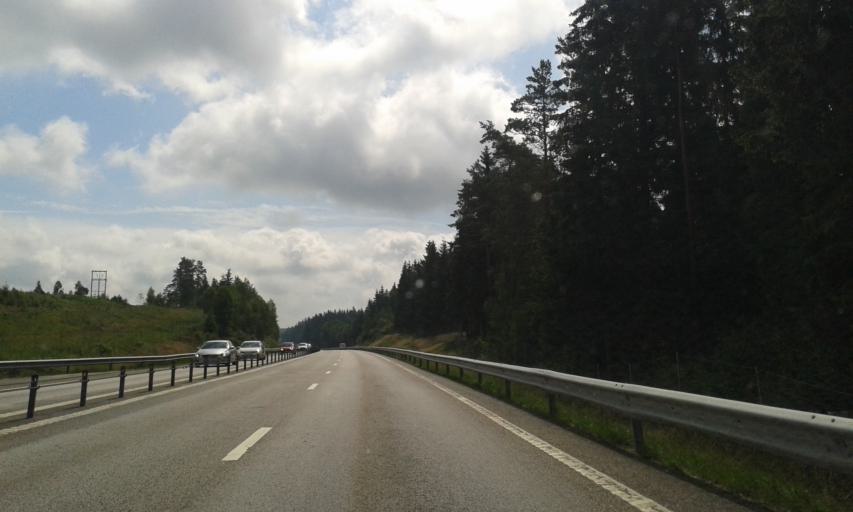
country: SE
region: Vaestra Goetaland
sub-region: Boras Kommun
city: Dalsjofors
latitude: 57.6146
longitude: 13.1166
